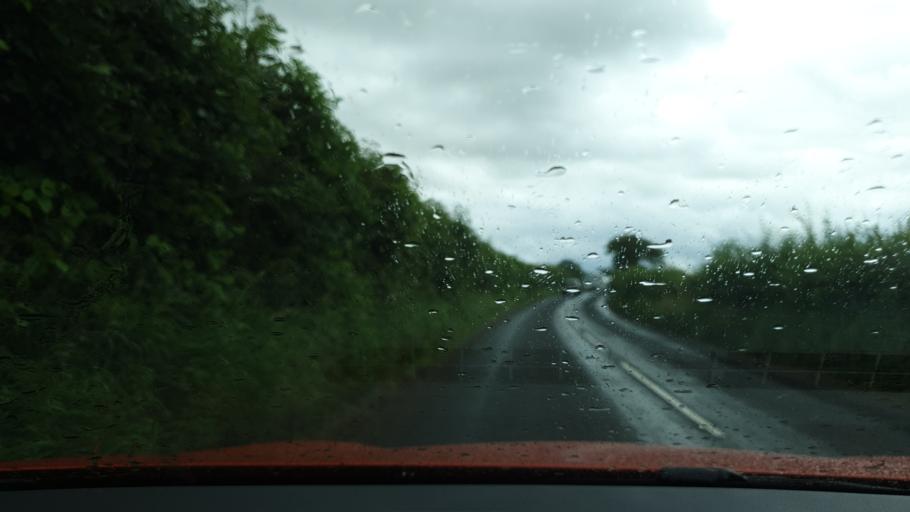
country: GB
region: England
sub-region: Cumbria
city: Penrith
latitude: 54.6246
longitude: -2.7959
